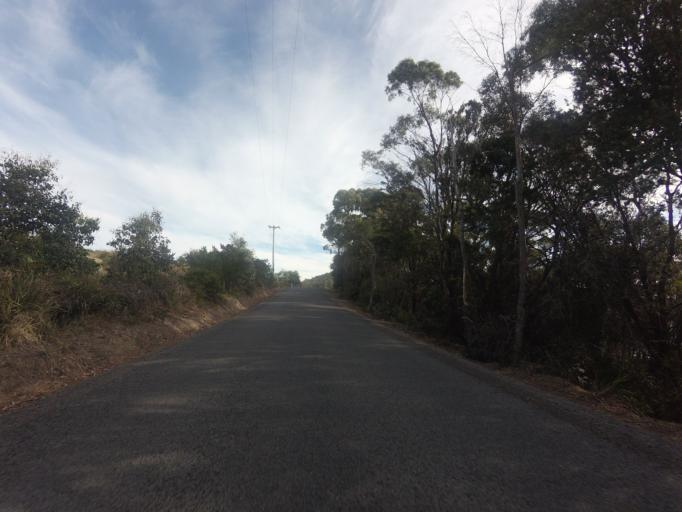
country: AU
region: Tasmania
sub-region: Sorell
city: Sorell
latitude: -42.9629
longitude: 147.8359
